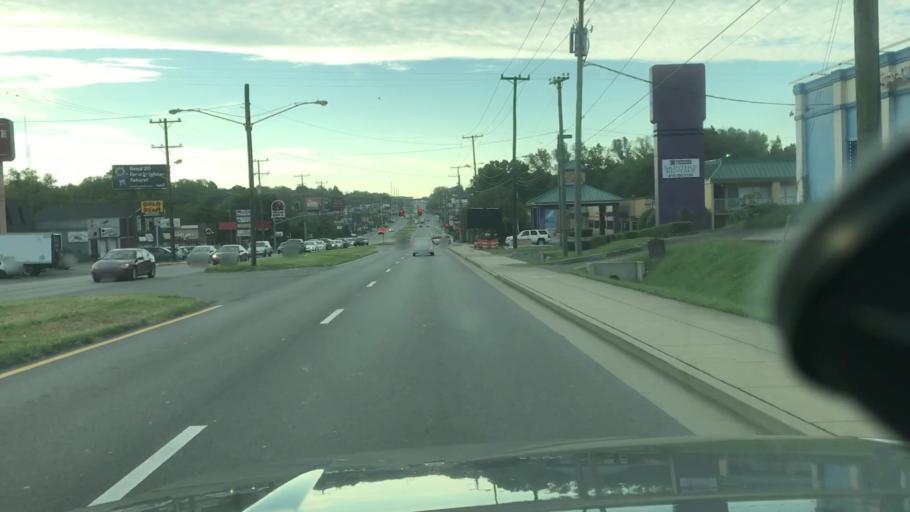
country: US
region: Tennessee
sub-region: Davidson County
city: Nashville
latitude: 36.1304
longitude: -86.7160
